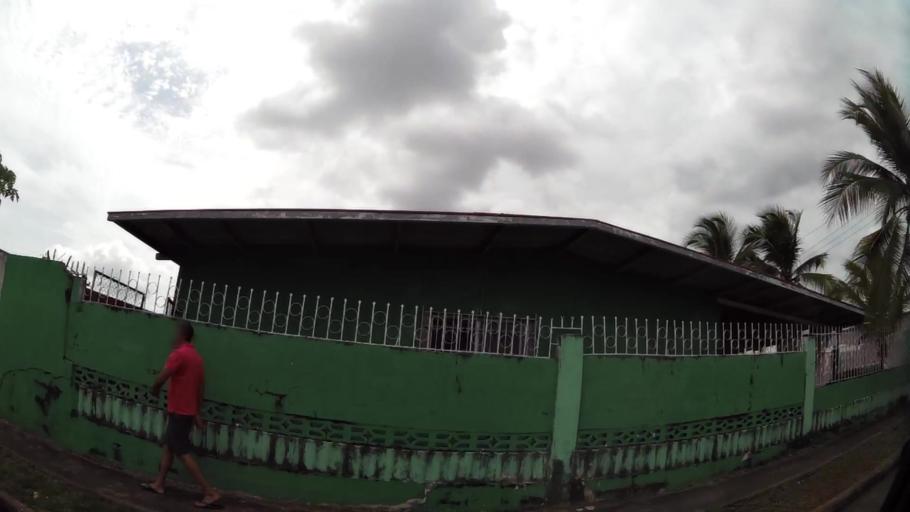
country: PA
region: Panama
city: San Miguelito
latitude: 9.0556
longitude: -79.4217
